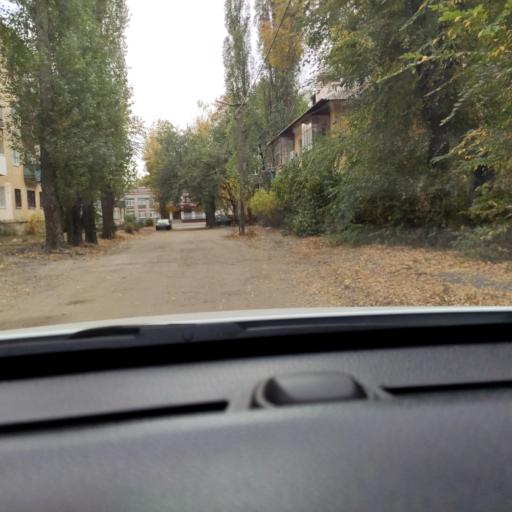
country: RU
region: Voronezj
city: Maslovka
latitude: 51.6146
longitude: 39.2528
